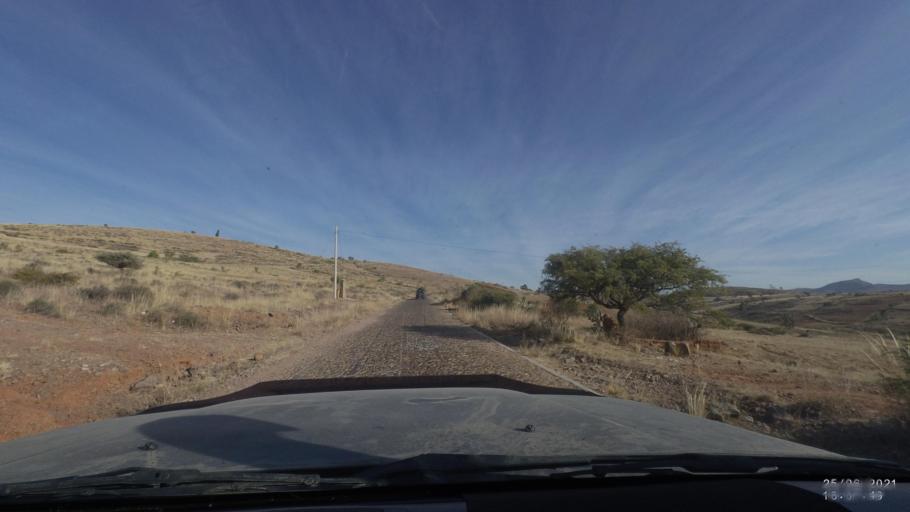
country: BO
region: Cochabamba
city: Cliza
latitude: -17.6779
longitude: -65.9038
